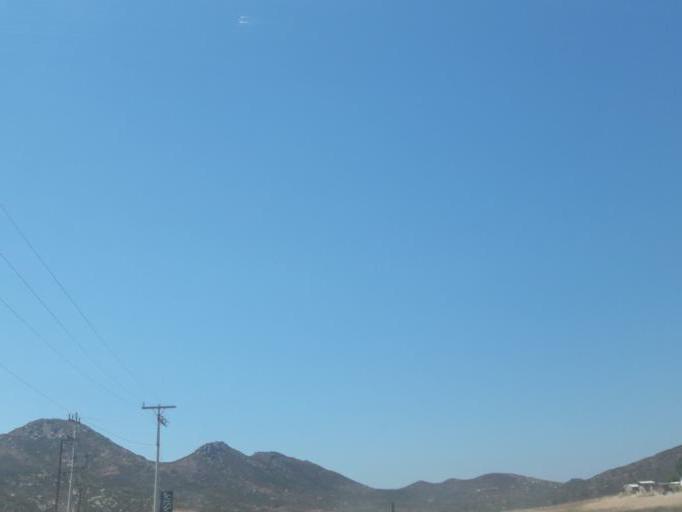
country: MX
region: Baja California
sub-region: Ensenada
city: Rancho Verde
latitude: 32.0931
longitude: -116.6319
